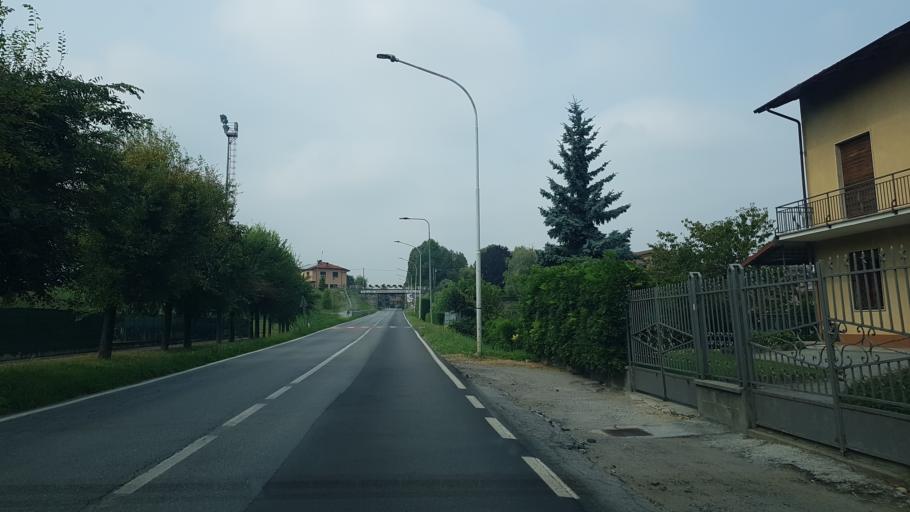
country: IT
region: Piedmont
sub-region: Provincia di Cuneo
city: Chiusa di Pesio
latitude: 44.3275
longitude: 7.6748
